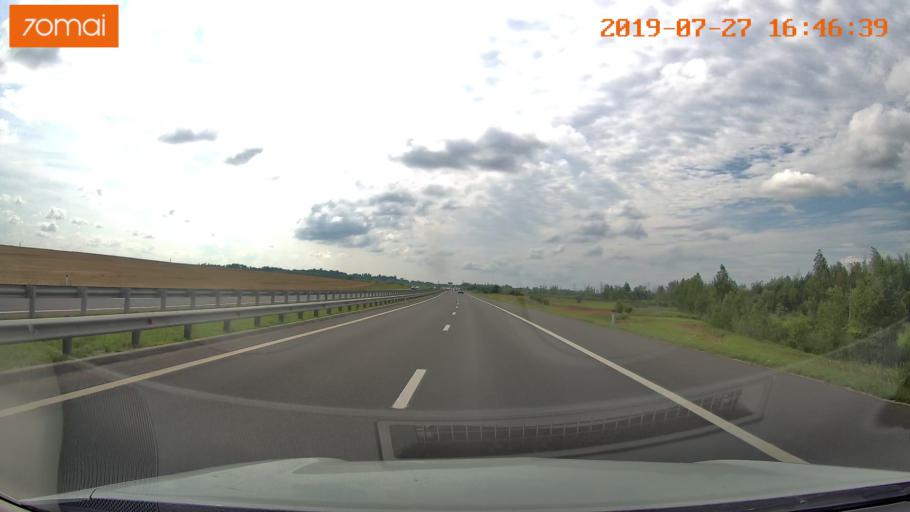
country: RU
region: Kaliningrad
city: Gvardeysk
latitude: 54.6677
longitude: 21.0160
